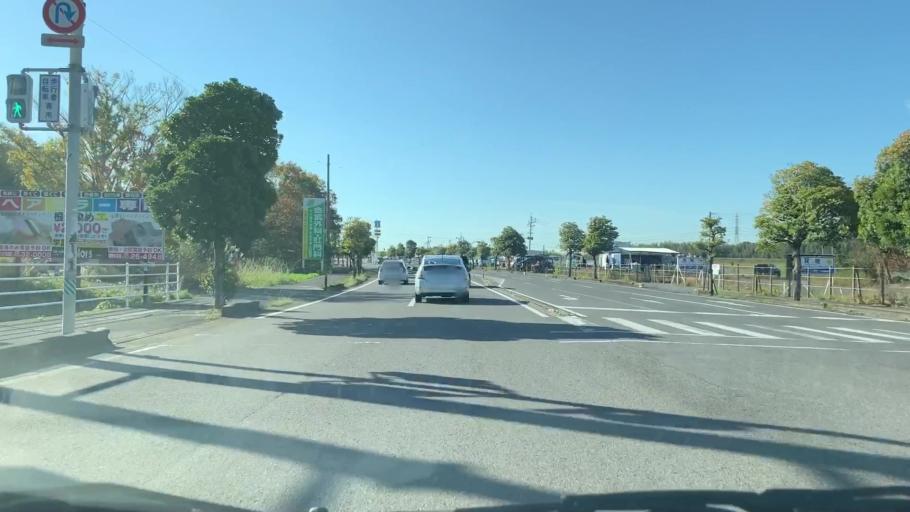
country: JP
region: Saga Prefecture
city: Saga-shi
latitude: 33.3147
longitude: 130.2759
